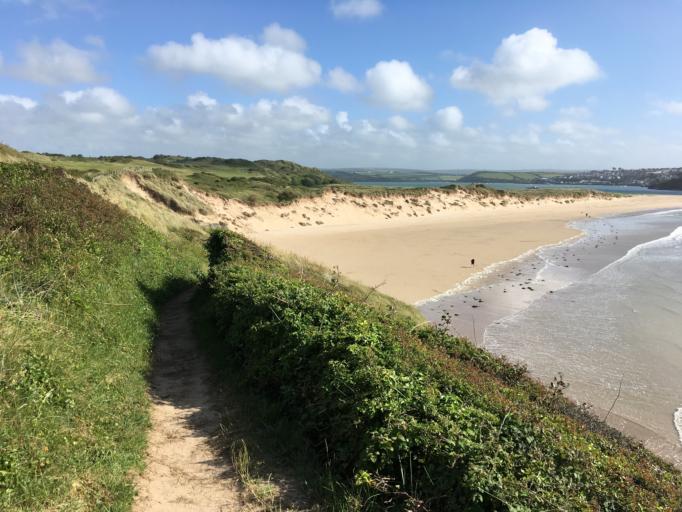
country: GB
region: England
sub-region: Cornwall
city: Polzeath
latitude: 50.5561
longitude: -4.9284
